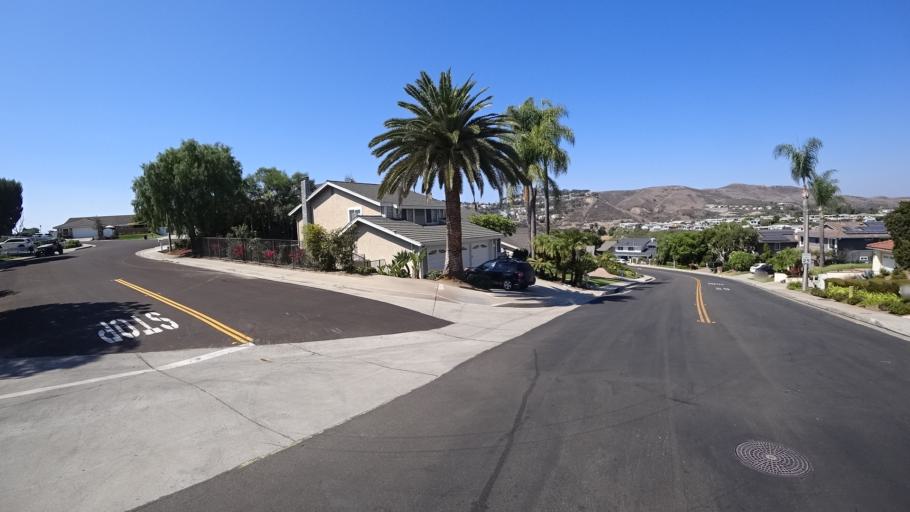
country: US
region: California
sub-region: Orange County
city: San Clemente
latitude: 33.4581
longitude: -117.6355
